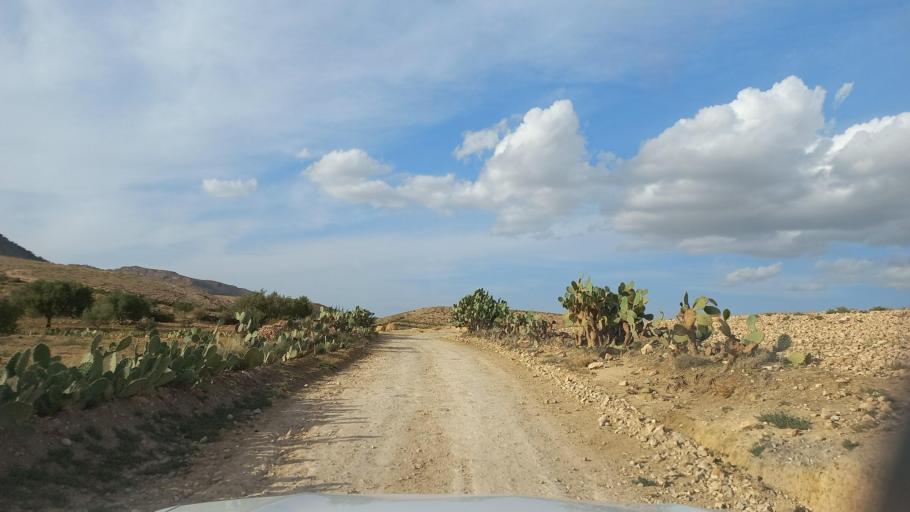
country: TN
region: Al Qasrayn
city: Sbiba
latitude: 35.4551
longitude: 9.0836
